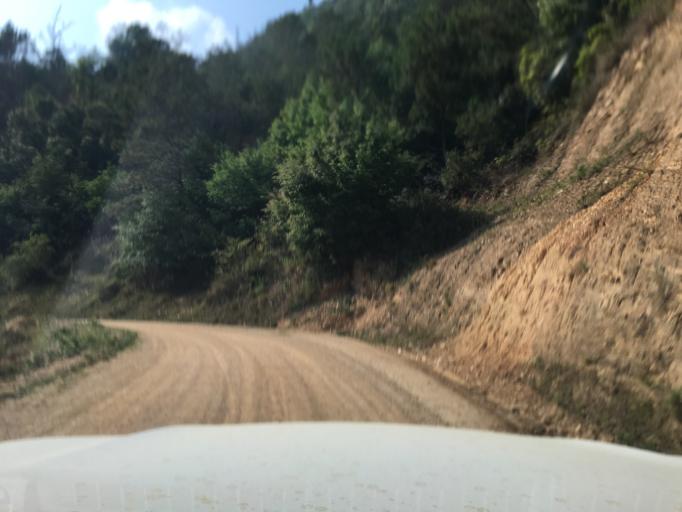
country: LA
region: Houaphan
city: Huameung
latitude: 20.2033
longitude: 103.8441
